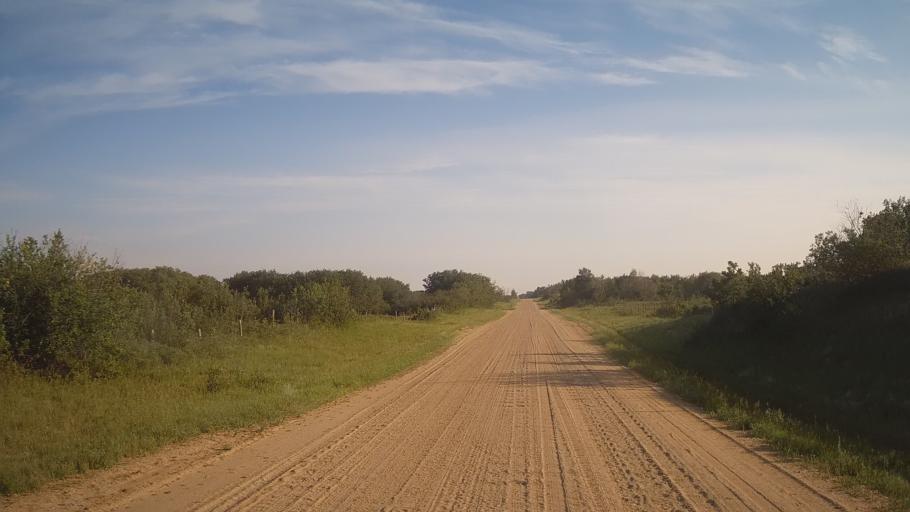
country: CA
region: Saskatchewan
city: Saskatoon
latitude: 51.8403
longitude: -106.5240
